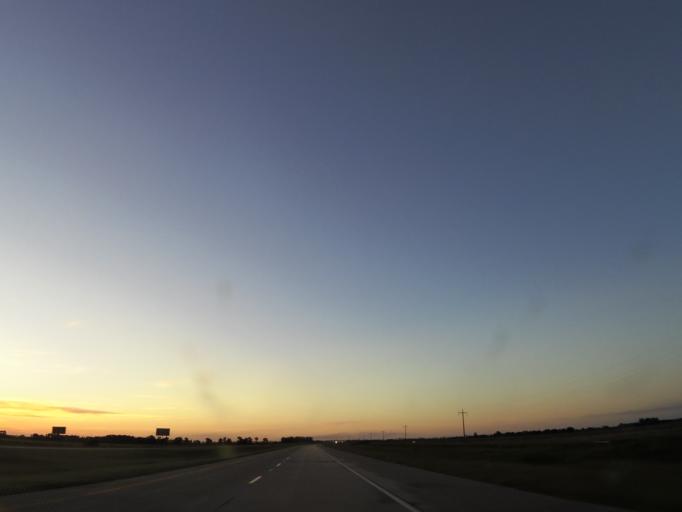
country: US
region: North Dakota
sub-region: Walsh County
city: Grafton
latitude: 48.3680
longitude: -97.1896
